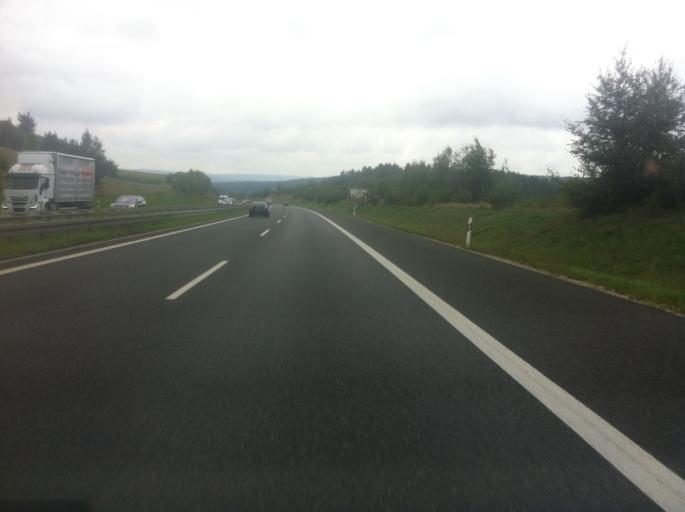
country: DE
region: Bavaria
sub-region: Upper Palatinate
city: Irchenrieth
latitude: 49.5670
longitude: 12.2150
